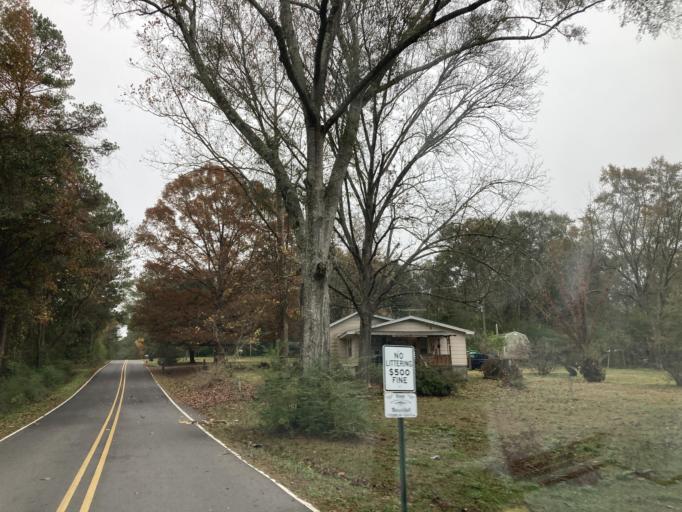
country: US
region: Mississippi
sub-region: Lamar County
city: Lumberton
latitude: 31.0650
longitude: -89.4221
